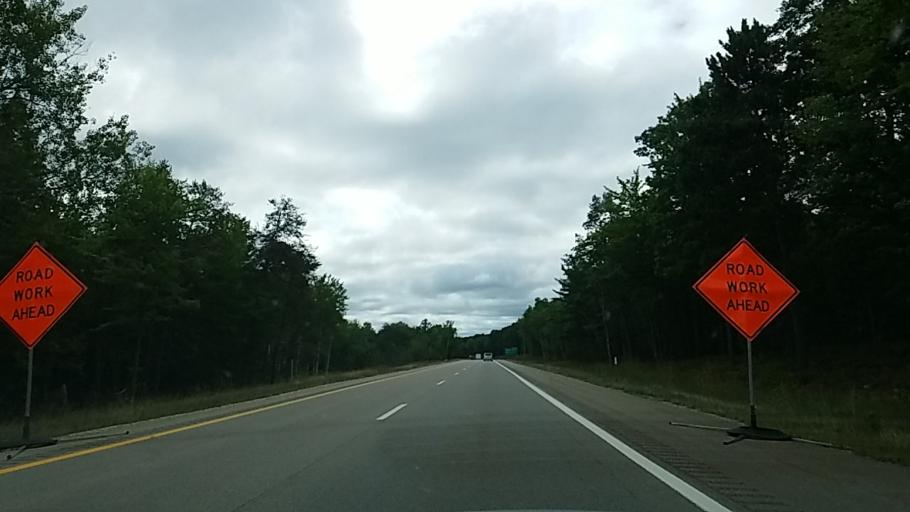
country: US
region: Michigan
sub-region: Crawford County
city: Grayling
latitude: 44.7370
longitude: -84.7096
